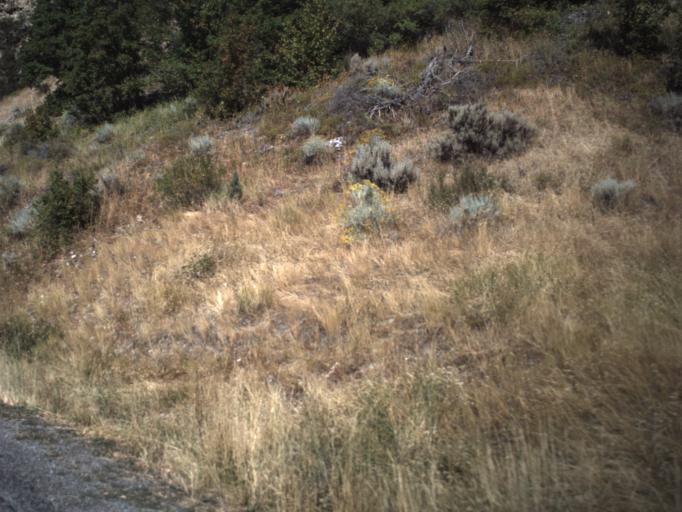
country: US
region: Utah
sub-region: Cache County
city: Millville
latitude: 41.6213
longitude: -111.7489
